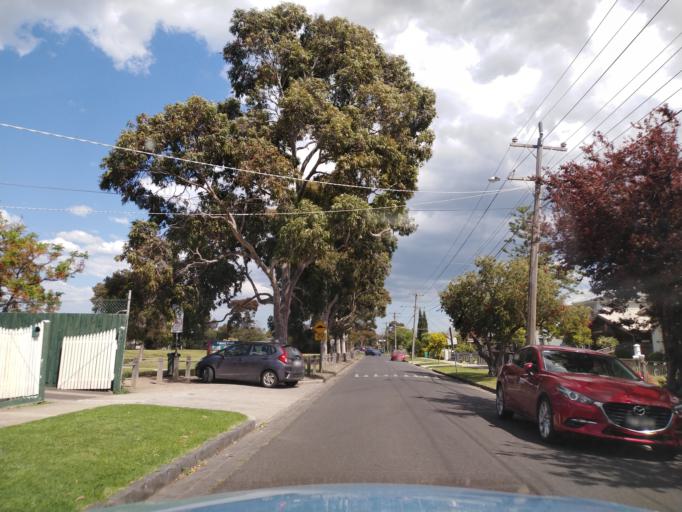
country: AU
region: Victoria
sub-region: Hobsons Bay
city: South Kingsville
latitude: -37.8378
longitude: 144.8680
